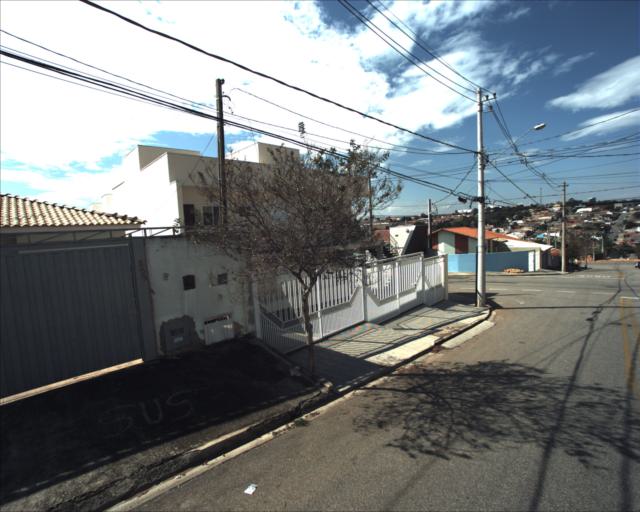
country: BR
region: Sao Paulo
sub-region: Sorocaba
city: Sorocaba
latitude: -23.4773
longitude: -47.5100
